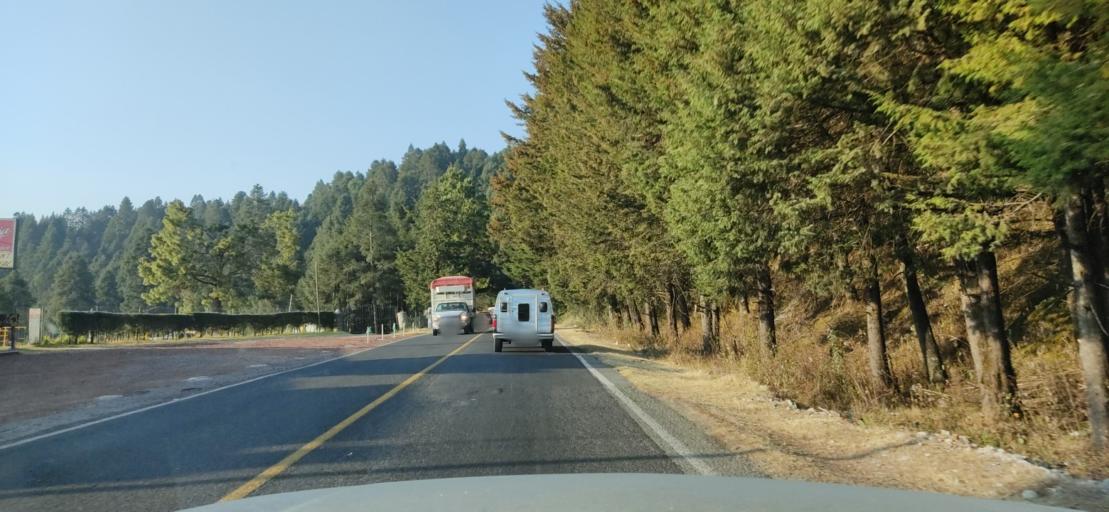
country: MX
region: Mexico
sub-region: Ocoyoacac
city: San Jeronimo Acazulco
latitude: 19.2485
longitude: -99.3722
